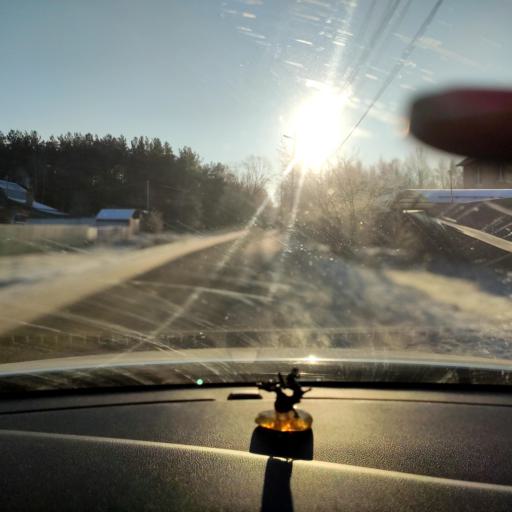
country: RU
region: Tatarstan
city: Stolbishchi
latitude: 55.6754
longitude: 49.1167
